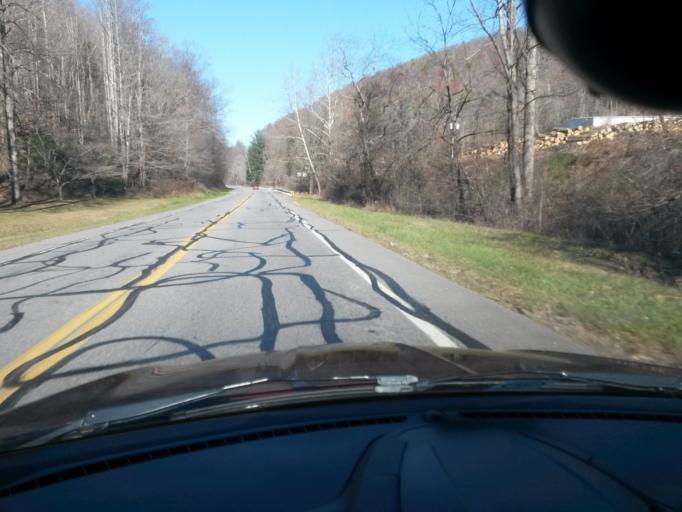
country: US
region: Virginia
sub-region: Patrick County
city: Stuart
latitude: 36.6688
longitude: -80.2743
